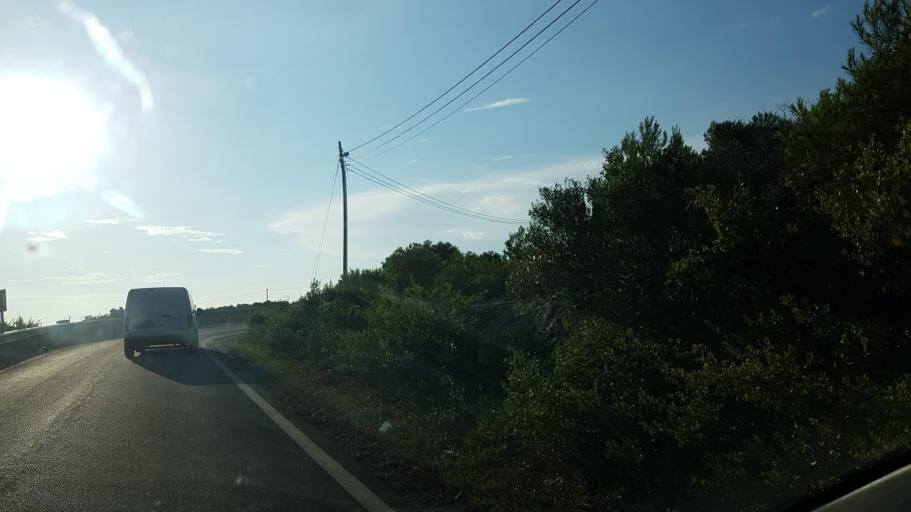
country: IT
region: Apulia
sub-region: Provincia di Lecce
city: Gemini
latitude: 39.8578
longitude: 18.2038
